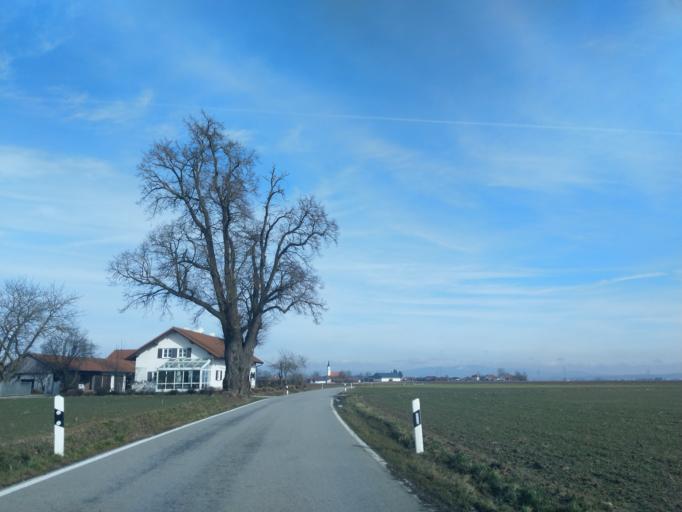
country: DE
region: Bavaria
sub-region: Lower Bavaria
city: Buchhofen
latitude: 48.6806
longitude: 12.9396
